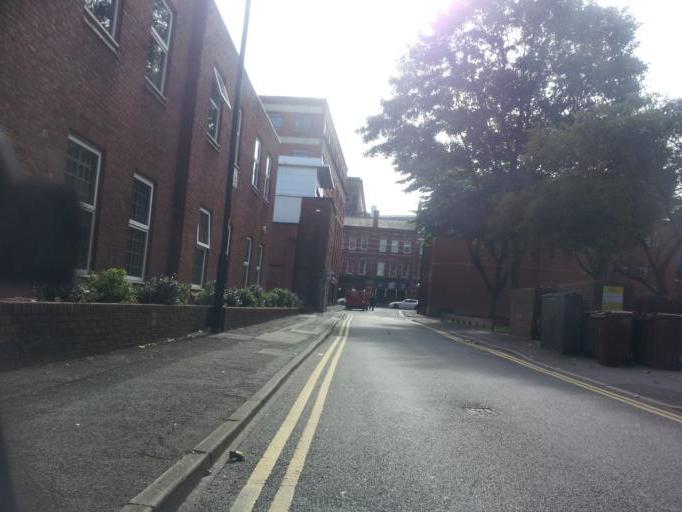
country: GB
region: England
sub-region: Manchester
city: Hulme
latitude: 53.4774
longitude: -2.2516
